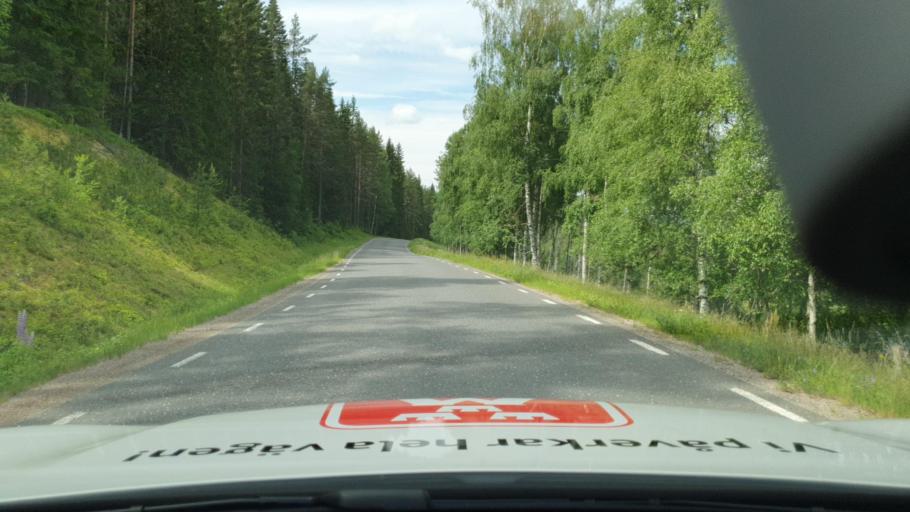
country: SE
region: Vaermland
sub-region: Torsby Kommun
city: Torsby
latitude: 60.6705
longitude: 12.6934
